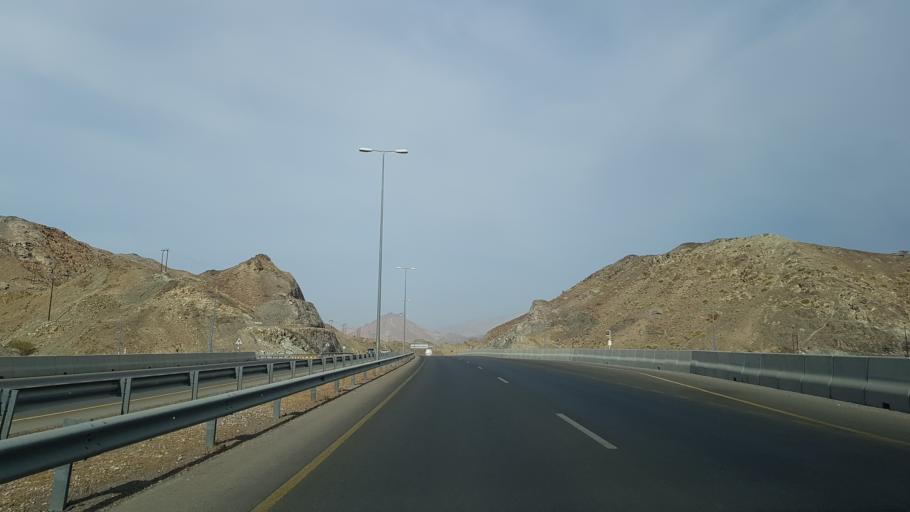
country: OM
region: Muhafazat ad Dakhiliyah
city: Bidbid
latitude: 23.4137
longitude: 58.0896
